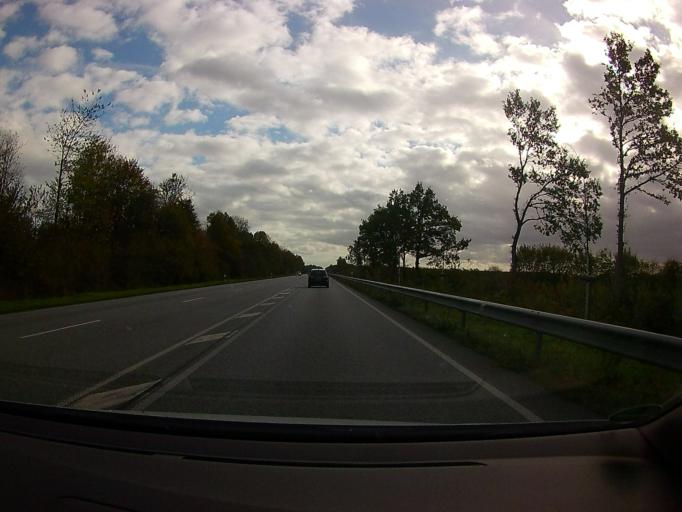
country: DE
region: Schleswig-Holstein
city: Kasseburg
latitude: 53.5664
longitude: 10.4052
